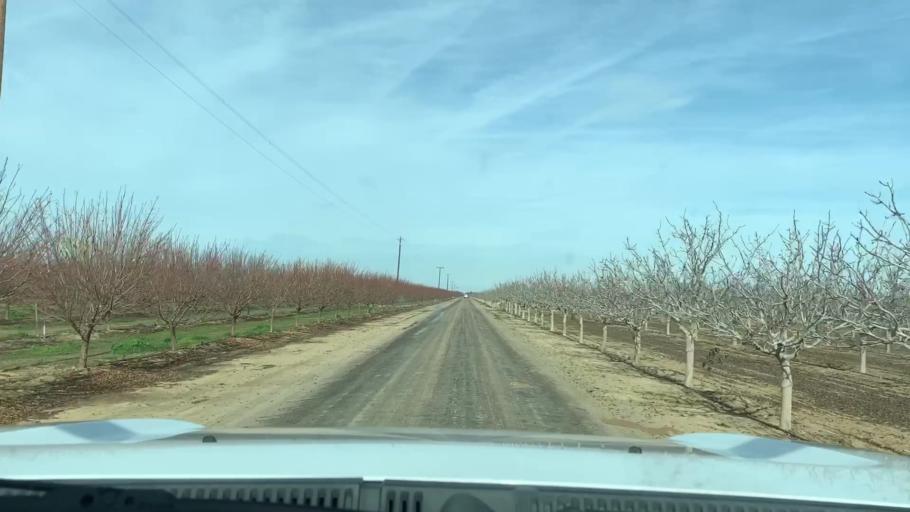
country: US
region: California
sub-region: Kern County
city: Lost Hills
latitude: 35.6039
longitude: -119.5357
